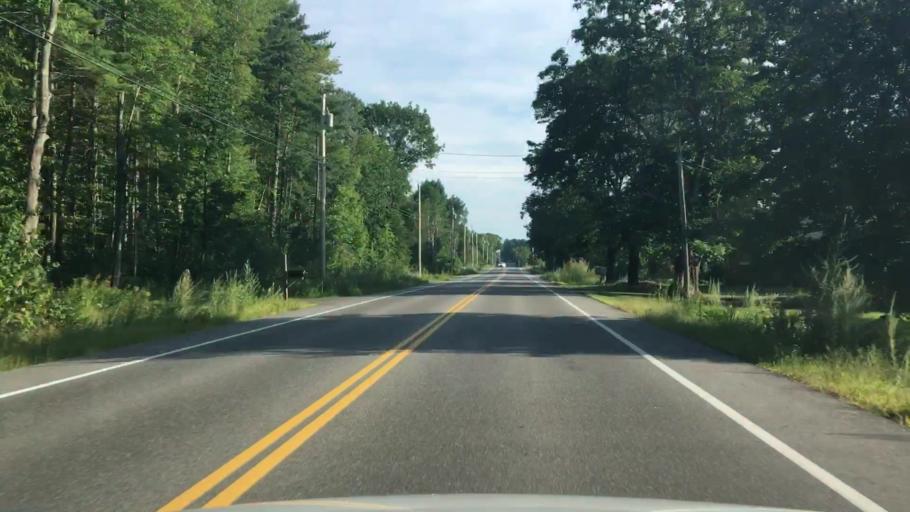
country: US
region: Maine
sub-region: Cumberland County
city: South Windham
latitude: 43.7827
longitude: -70.4397
